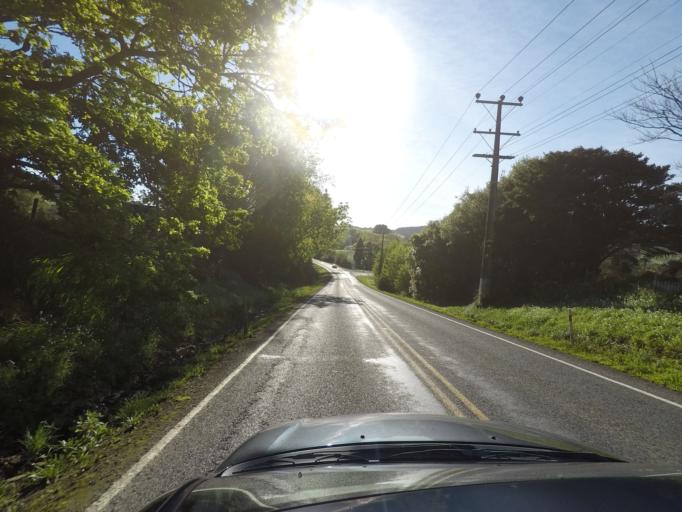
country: NZ
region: Auckland
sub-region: Auckland
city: Red Hill
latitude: -36.9974
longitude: 174.9765
